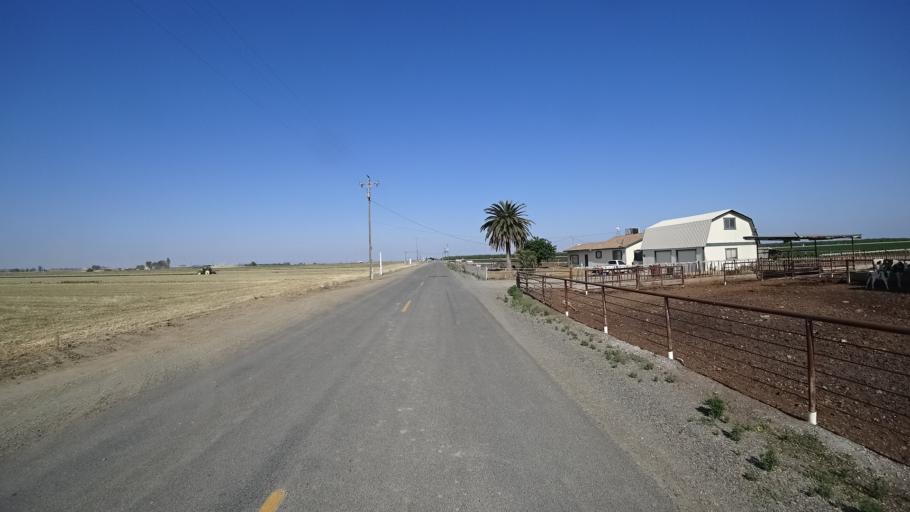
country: US
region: California
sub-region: Kings County
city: Home Garden
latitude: 36.2404
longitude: -119.5944
